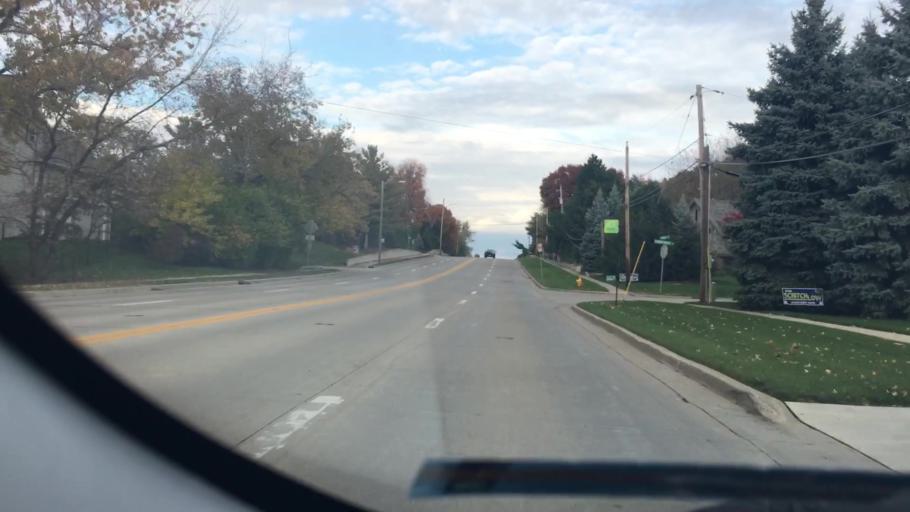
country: US
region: Illinois
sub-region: McLean County
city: Bloomington
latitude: 40.4955
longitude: -88.9629
